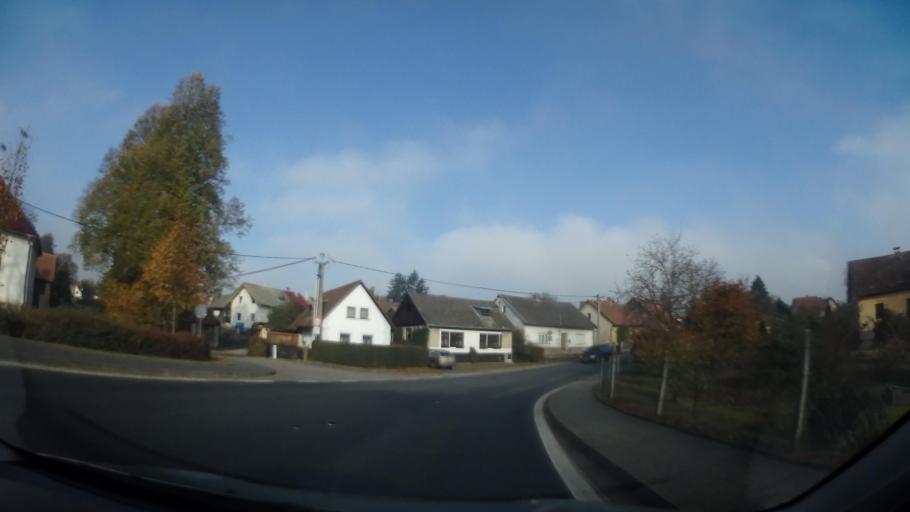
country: CZ
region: Vysocina
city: Krizanov
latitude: 49.4404
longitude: 16.1419
